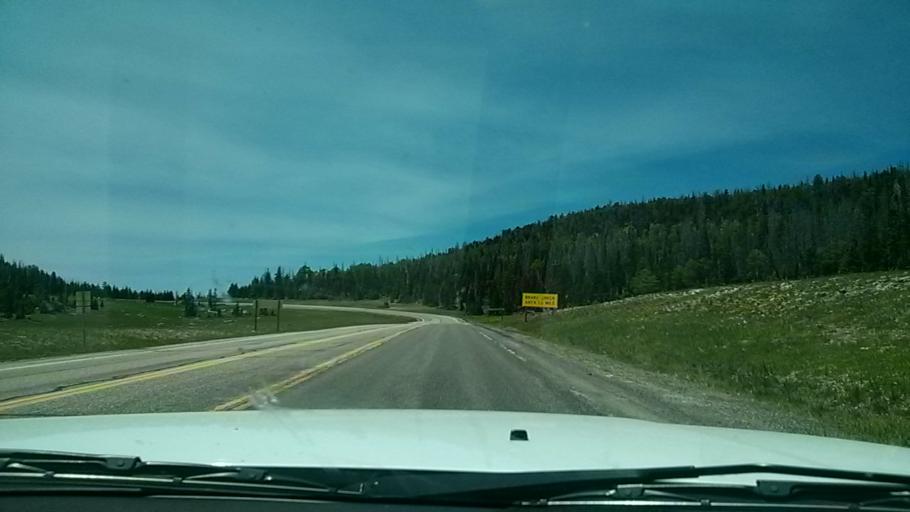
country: US
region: Utah
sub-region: Iron County
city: Cedar City
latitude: 37.5718
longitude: -112.8377
